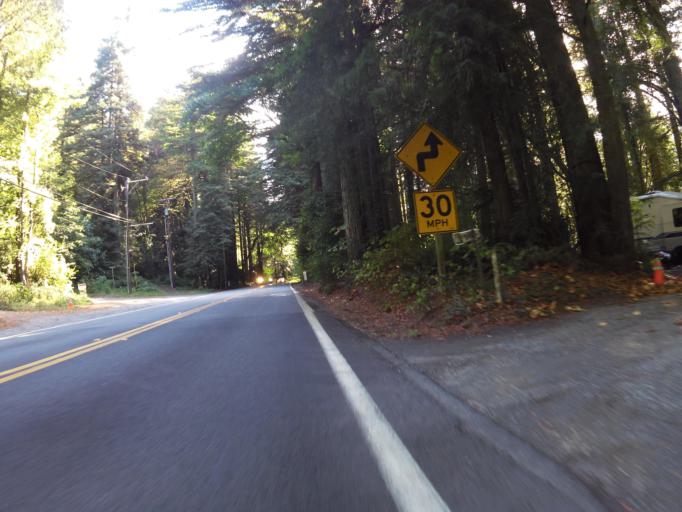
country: US
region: California
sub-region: Del Norte County
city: Bertsch-Oceanview
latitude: 41.8540
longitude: -124.1204
